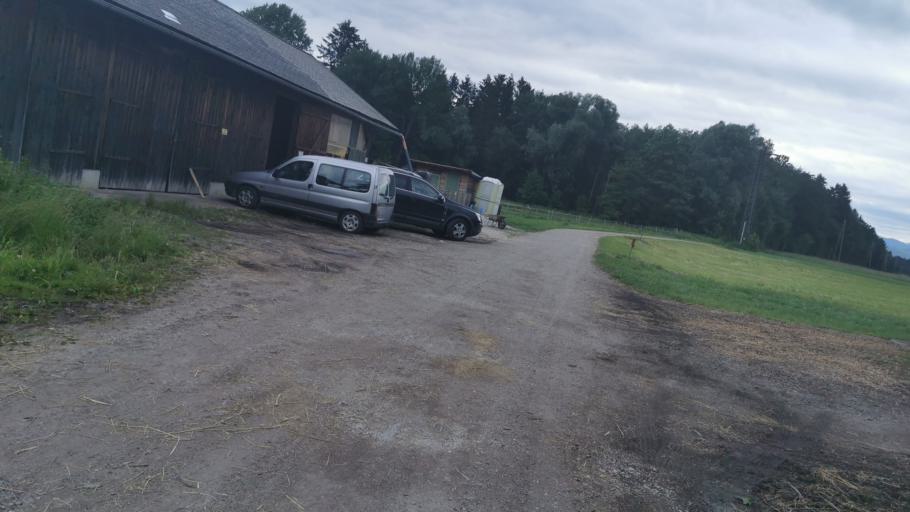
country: DE
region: Bavaria
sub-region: Upper Bavaria
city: Ainring
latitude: 47.7689
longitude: 12.9719
